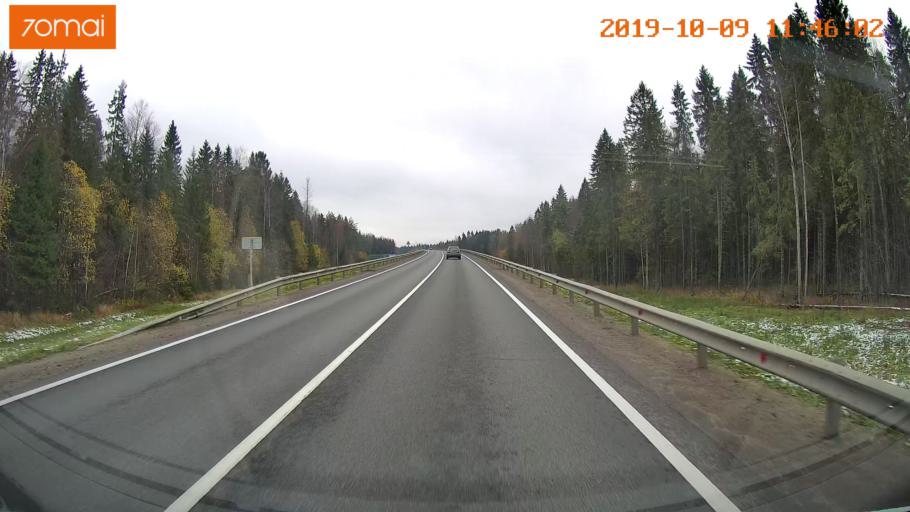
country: RU
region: Vologda
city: Gryazovets
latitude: 58.8599
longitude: 40.1992
